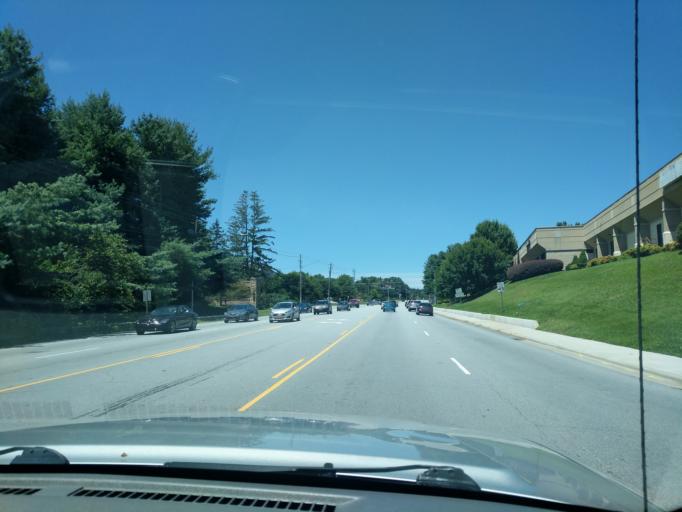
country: US
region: North Carolina
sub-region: Buncombe County
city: Biltmore Forest
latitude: 35.5065
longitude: -82.5252
